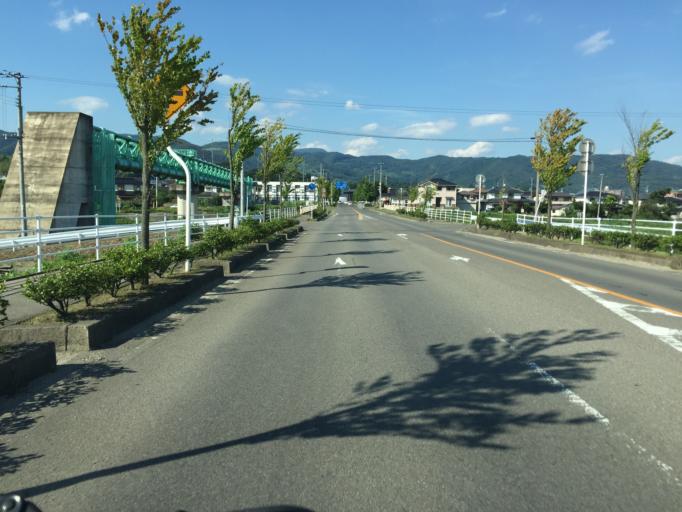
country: JP
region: Fukushima
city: Fukushima-shi
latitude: 37.8236
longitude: 140.4442
